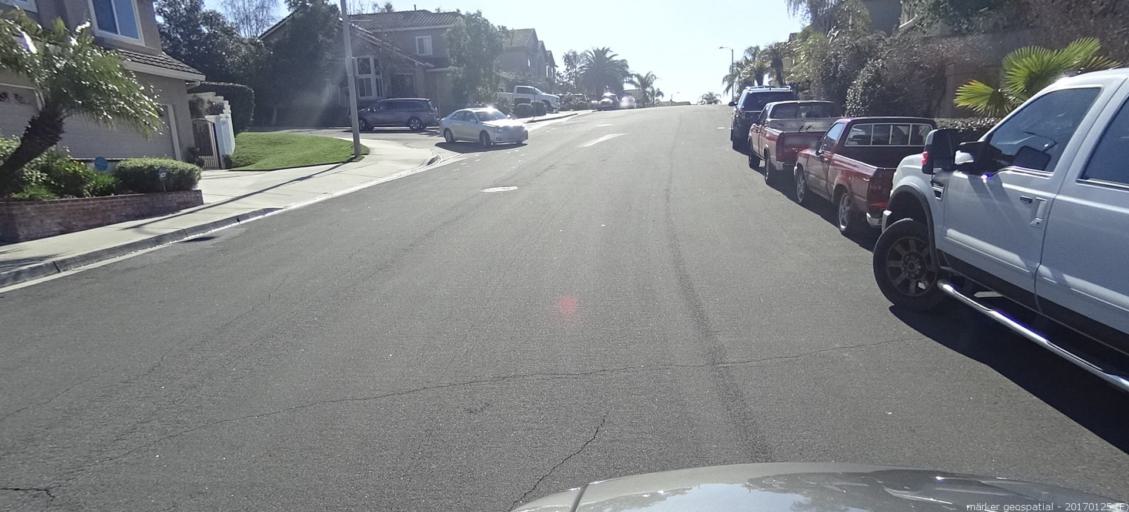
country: US
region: California
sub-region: Orange County
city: Portola Hills
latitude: 33.6848
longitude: -117.6338
